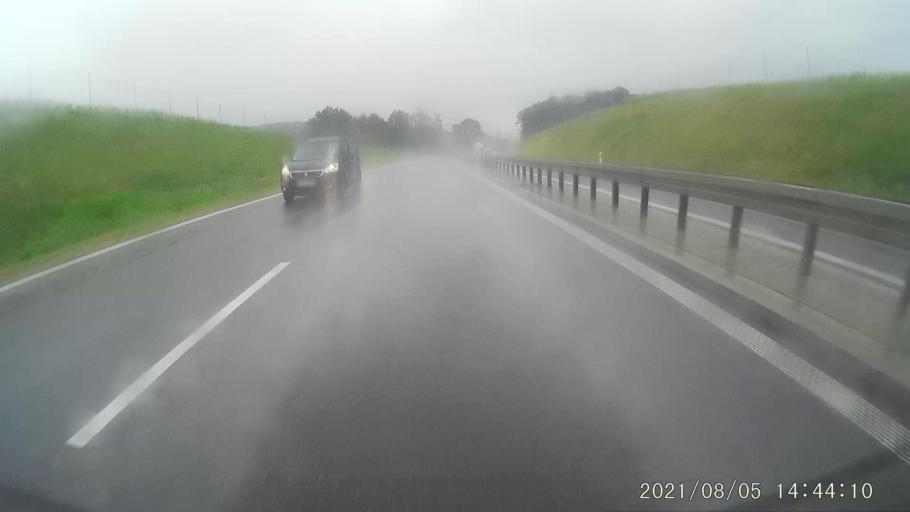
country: PL
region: Opole Voivodeship
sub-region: Powiat nyski
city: Nysa
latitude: 50.4919
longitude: 17.3829
